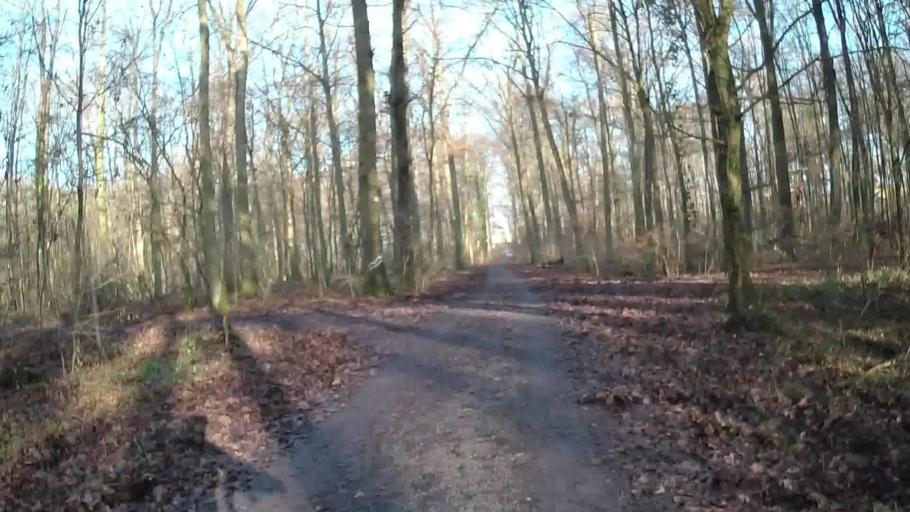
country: DE
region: Baden-Wuerttemberg
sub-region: Karlsruhe Region
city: Walldorf
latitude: 49.2819
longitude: 8.6451
